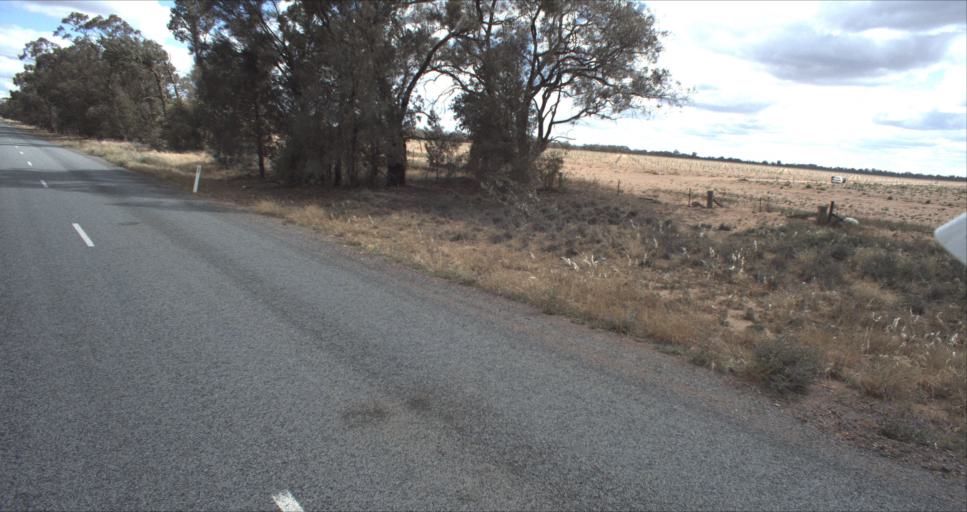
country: AU
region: New South Wales
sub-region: Leeton
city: Leeton
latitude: -34.6617
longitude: 146.3492
